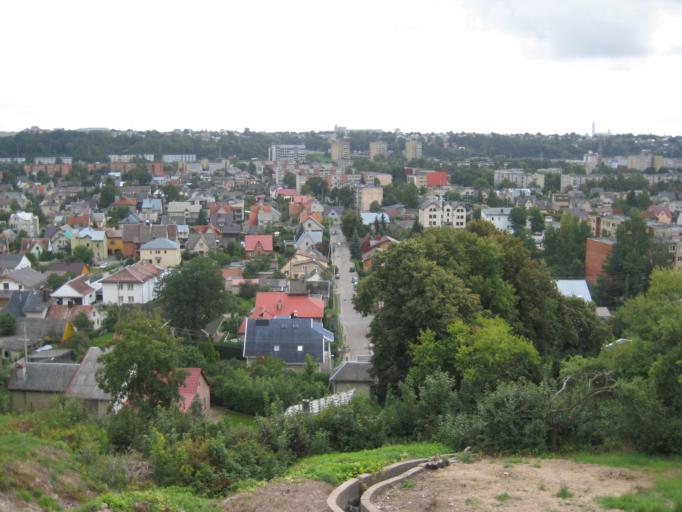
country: LT
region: Kauno apskritis
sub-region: Kaunas
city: Silainiai
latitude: 54.9223
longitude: 23.8939
